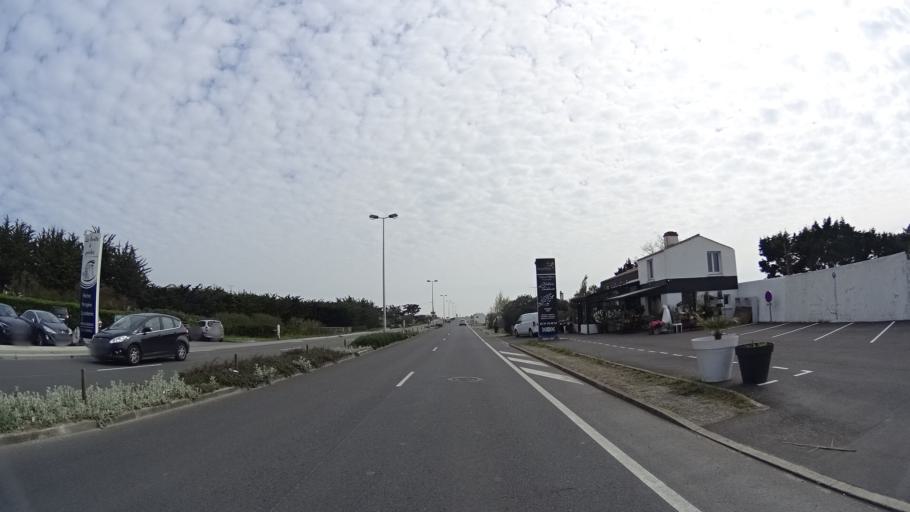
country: FR
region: Pays de la Loire
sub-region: Departement de la Vendee
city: La Gueriniere
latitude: 46.9962
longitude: -2.2476
